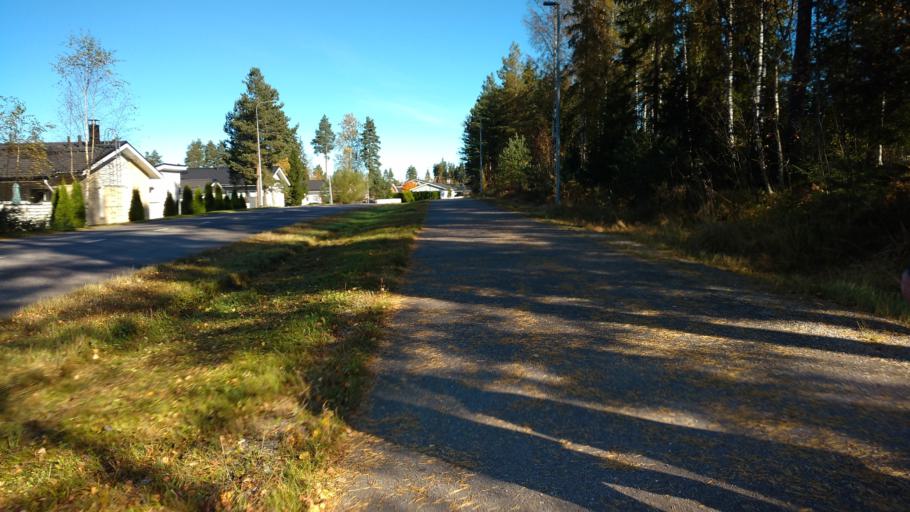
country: FI
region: Varsinais-Suomi
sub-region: Salo
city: Salo
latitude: 60.3995
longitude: 23.1842
